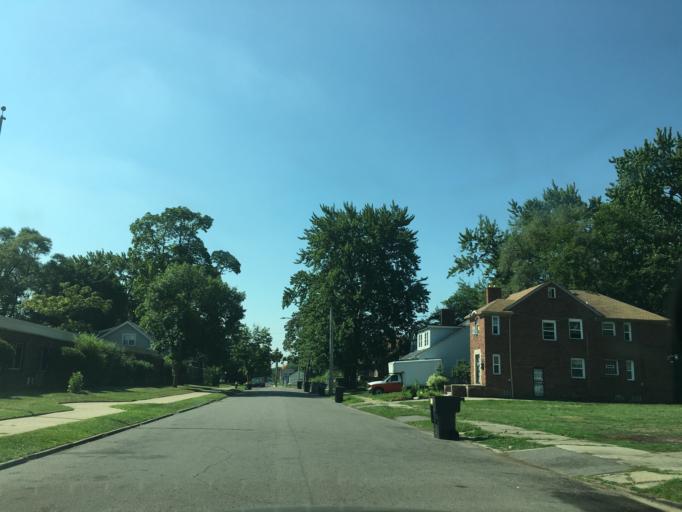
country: US
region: Michigan
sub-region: Wayne County
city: Highland Park
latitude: 42.4041
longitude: -83.1437
